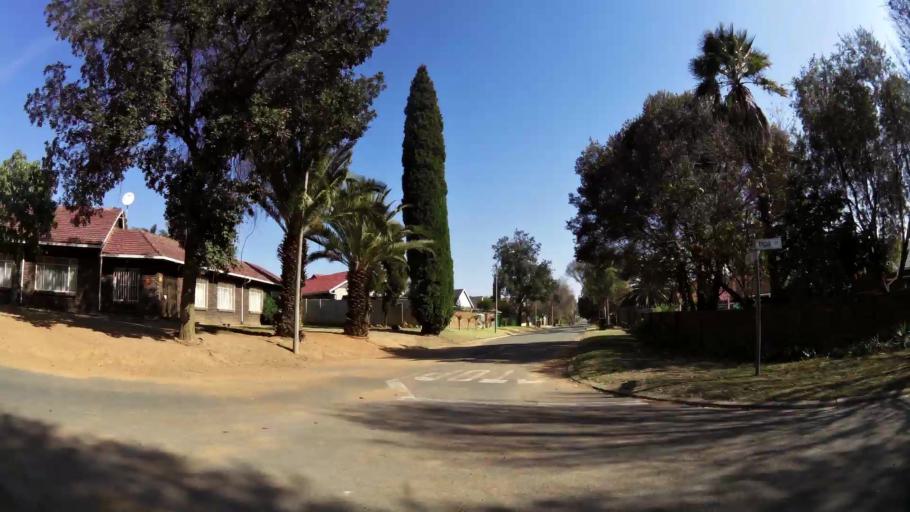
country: ZA
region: Gauteng
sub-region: Ekurhuleni Metropolitan Municipality
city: Tembisa
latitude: -26.0442
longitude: 28.2364
